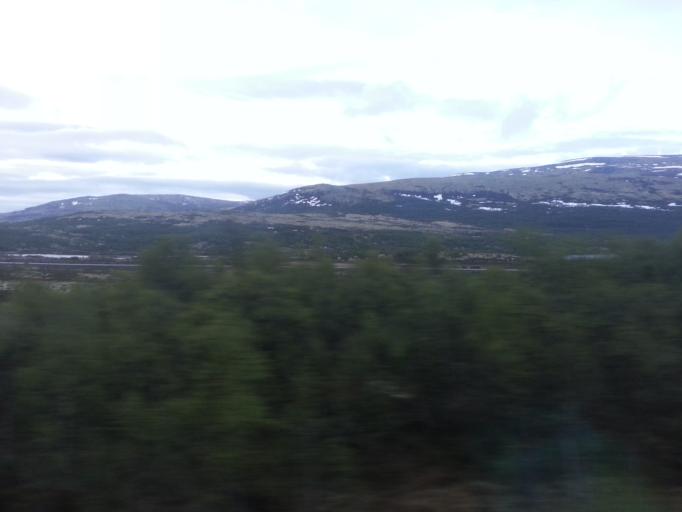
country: NO
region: Oppland
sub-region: Dovre
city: Dovre
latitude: 62.1849
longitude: 9.4728
